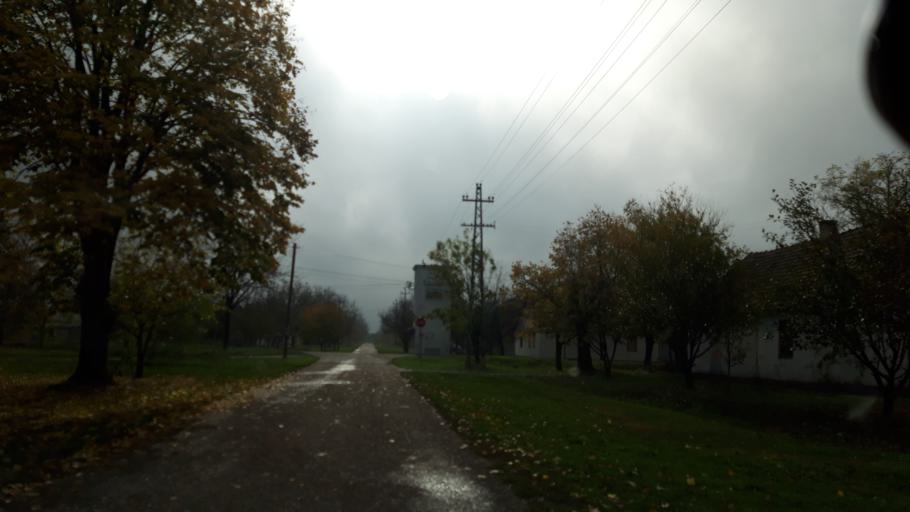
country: RS
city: Backo Gradiste
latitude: 45.5077
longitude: 19.9312
